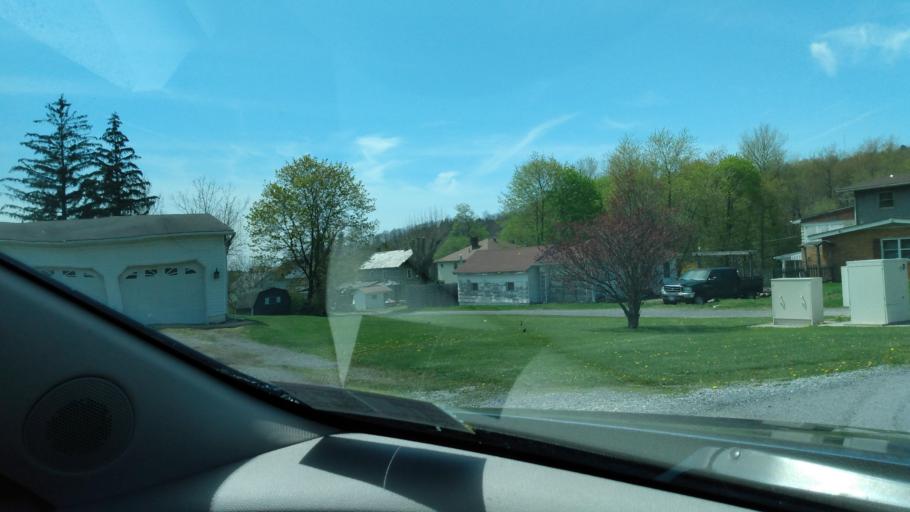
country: US
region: Pennsylvania
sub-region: Blair County
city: Bellwood
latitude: 40.6830
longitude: -78.4176
